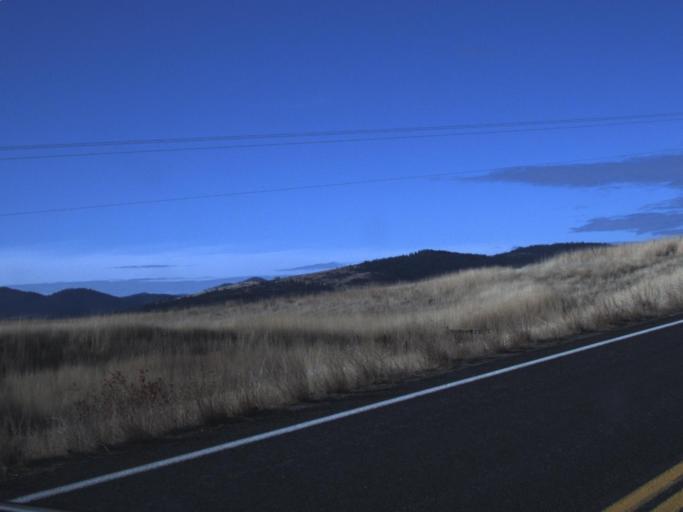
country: US
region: Washington
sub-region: Stevens County
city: Kettle Falls
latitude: 48.1618
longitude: -118.1705
